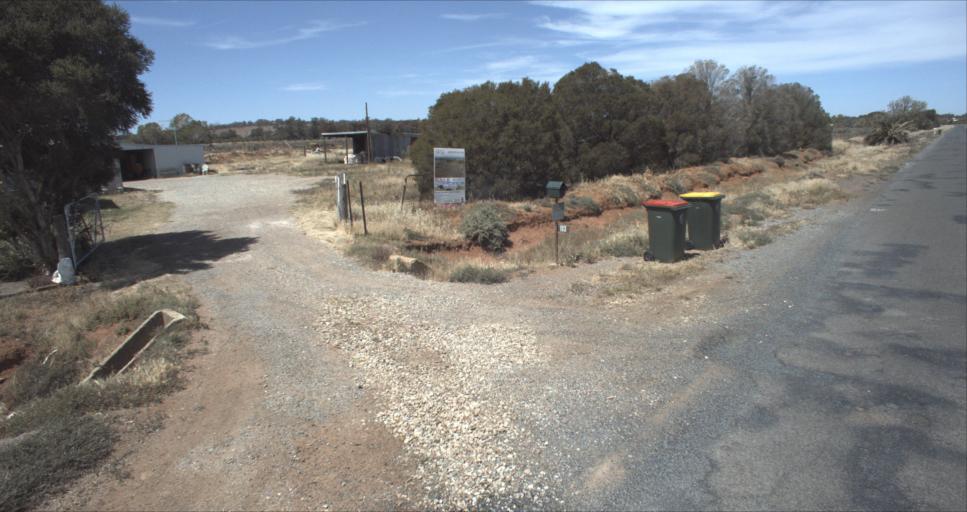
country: AU
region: New South Wales
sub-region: Leeton
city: Leeton
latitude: -34.6020
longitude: 146.4268
